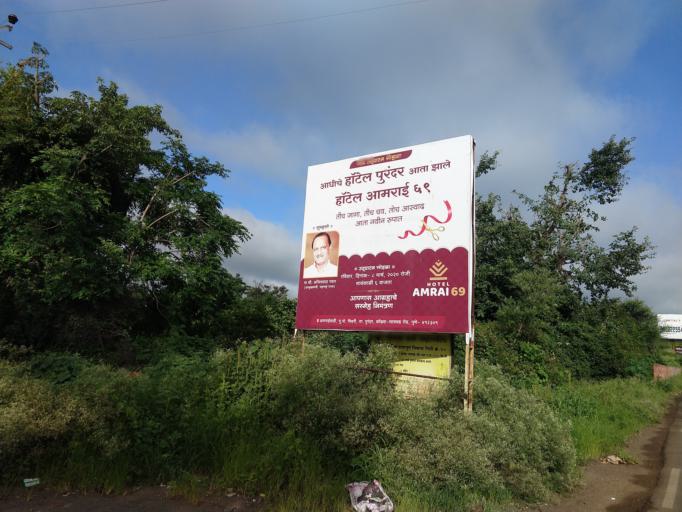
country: IN
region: Maharashtra
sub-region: Pune Division
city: Khed
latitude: 18.3941
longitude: 73.9188
